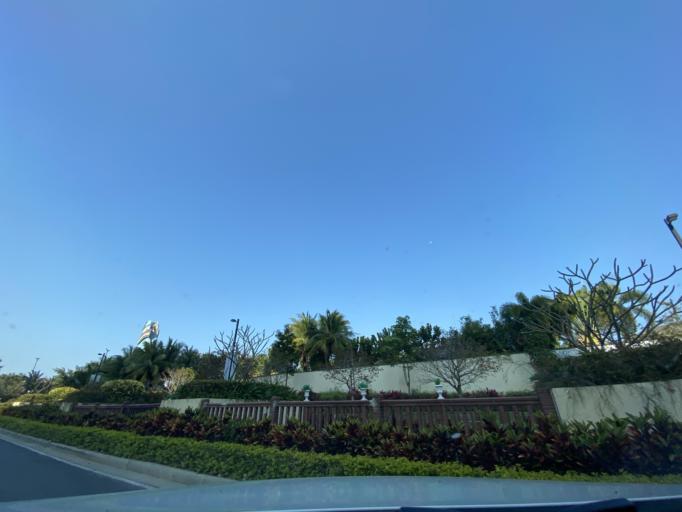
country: CN
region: Hainan
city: Xincun
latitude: 18.4210
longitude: 109.9425
